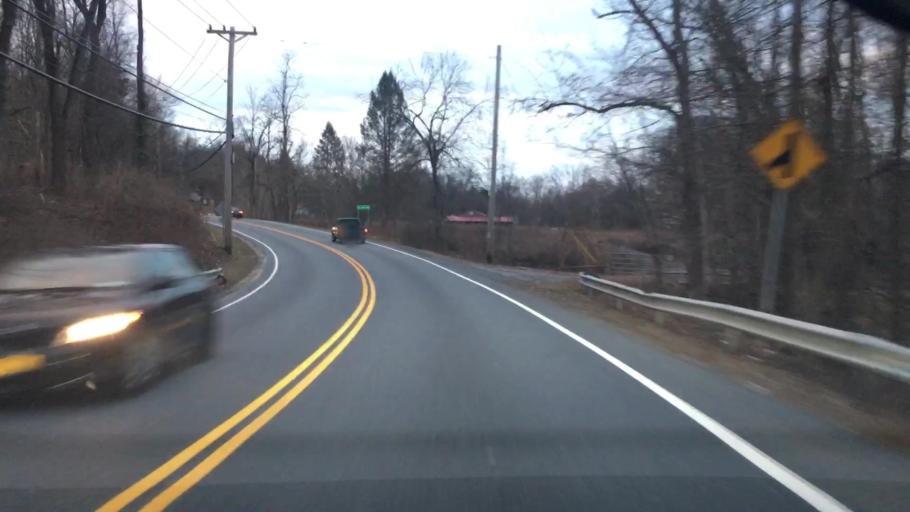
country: US
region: New York
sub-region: Dutchess County
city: Red Oaks Mill
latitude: 41.6600
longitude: -73.8673
